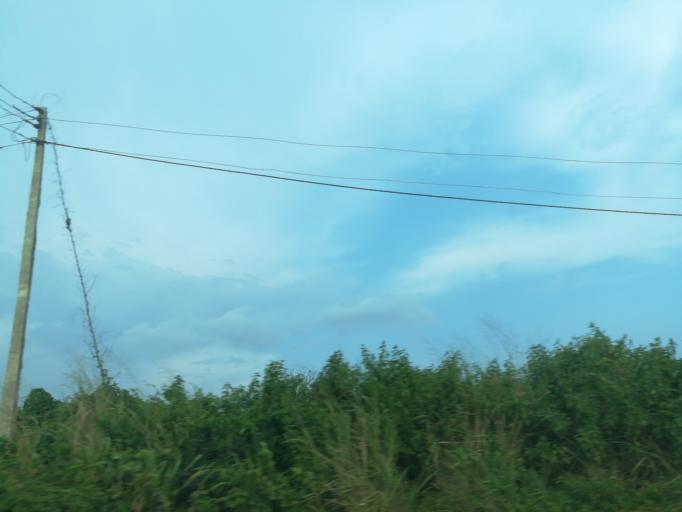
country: NG
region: Lagos
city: Ikorodu
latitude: 6.6352
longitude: 3.6698
